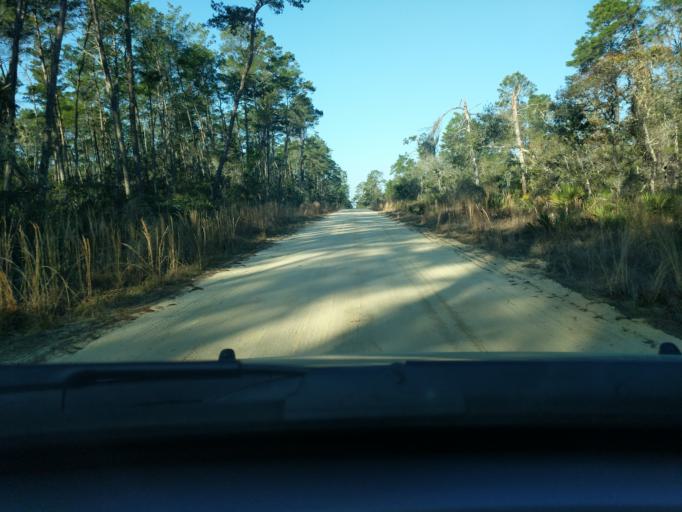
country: US
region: Florida
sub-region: Marion County
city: Silver Springs Shores
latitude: 29.2264
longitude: -81.8150
